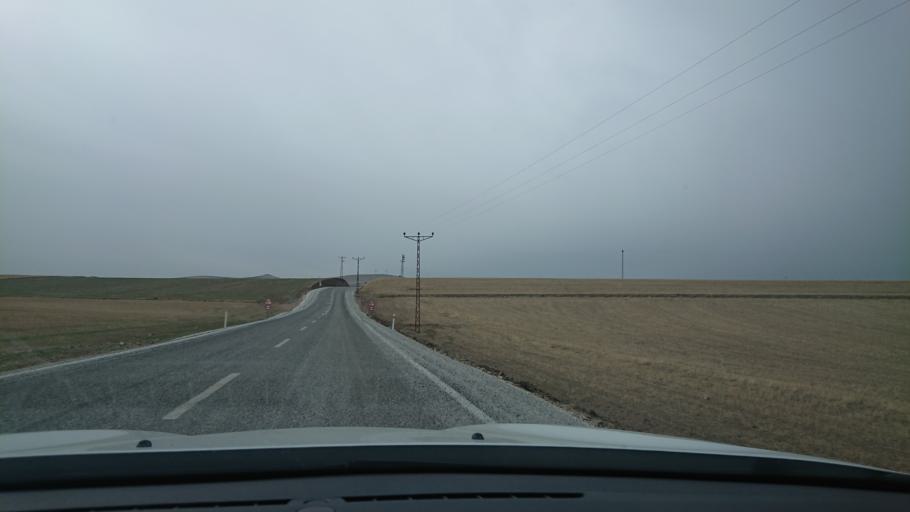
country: TR
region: Aksaray
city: Agacoren
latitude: 38.9227
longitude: 33.9408
